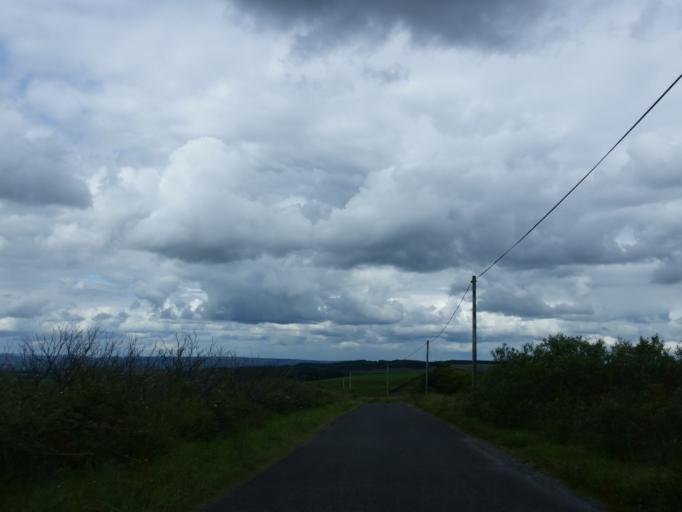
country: IE
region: Ulster
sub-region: County Monaghan
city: Clones
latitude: 54.2708
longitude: -7.2742
